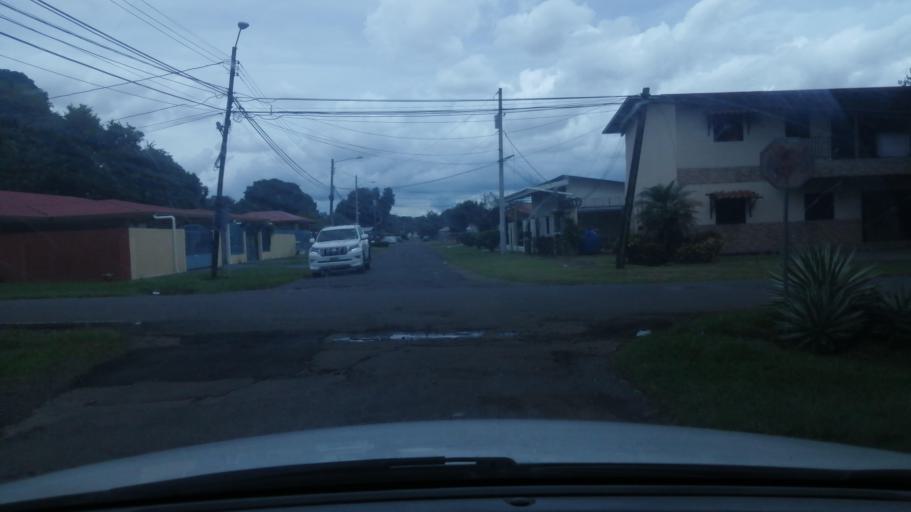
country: PA
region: Chiriqui
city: David
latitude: 8.4418
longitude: -82.4283
